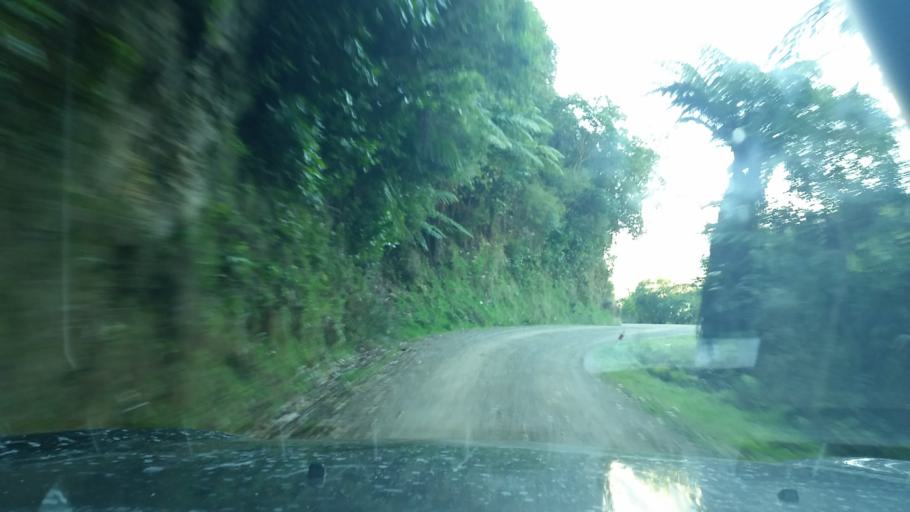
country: NZ
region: Marlborough
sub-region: Marlborough District
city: Picton
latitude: -41.0270
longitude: 174.1493
